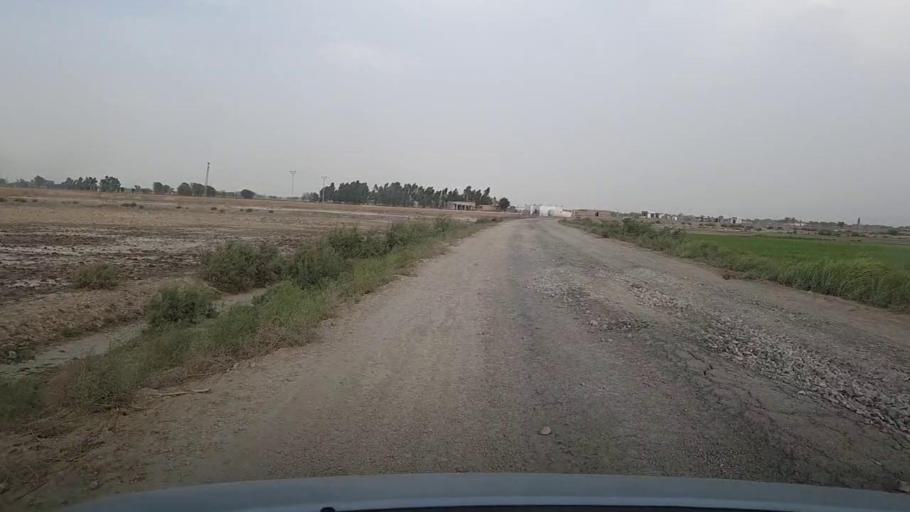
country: PK
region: Sindh
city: Dadu
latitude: 26.8125
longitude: 67.7764
